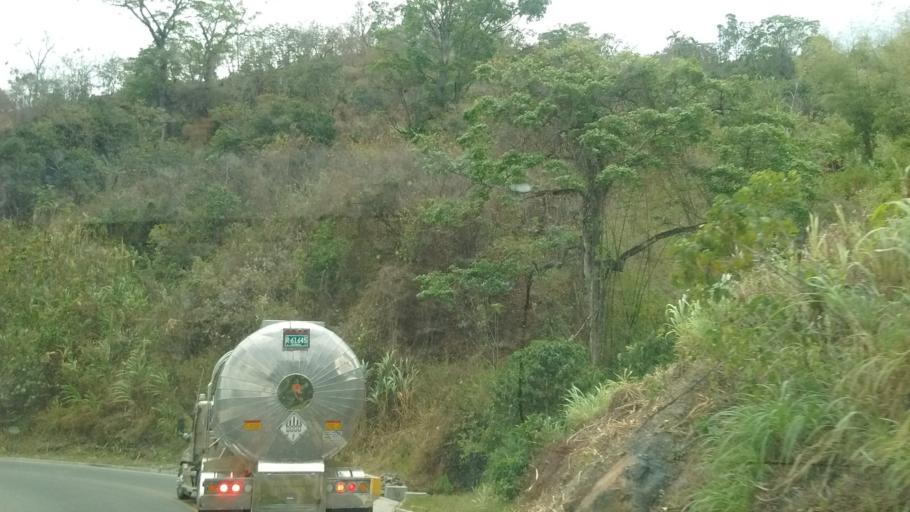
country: CO
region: Cauca
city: Rosas
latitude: 2.2930
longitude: -76.7076
